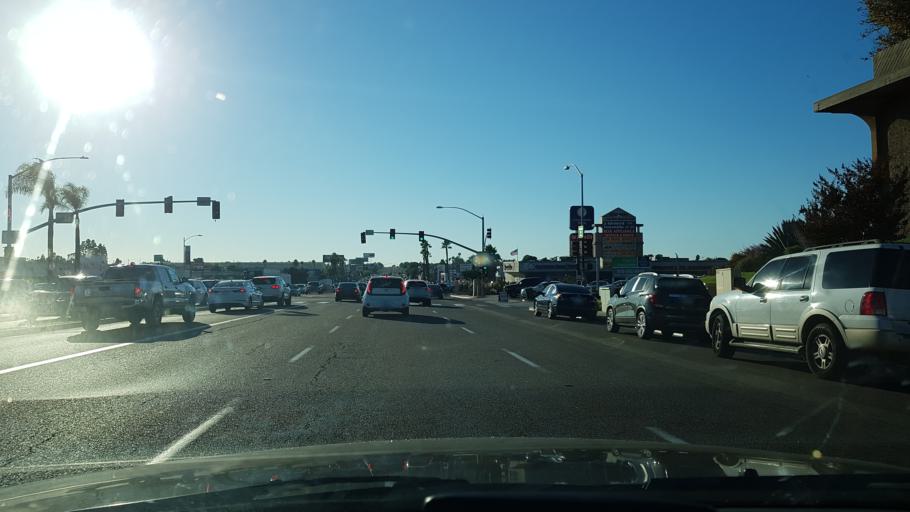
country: US
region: California
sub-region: San Diego County
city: San Diego
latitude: 32.8329
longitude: -117.1450
